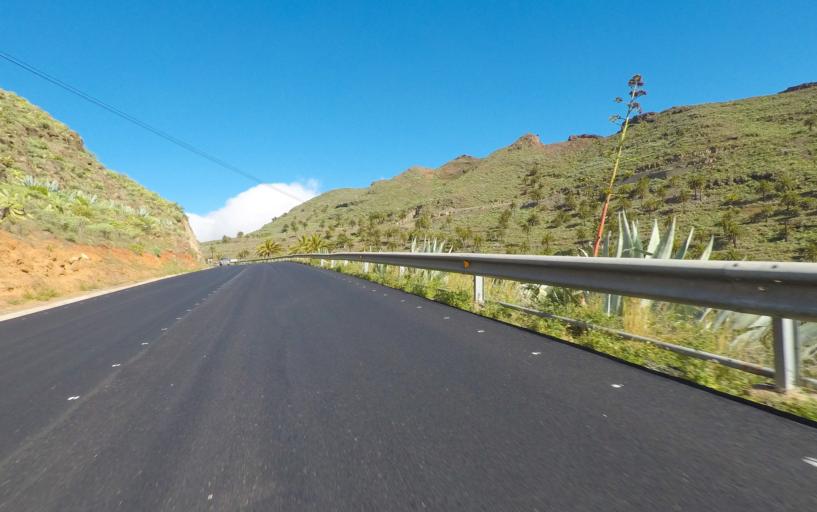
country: ES
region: Canary Islands
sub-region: Provincia de Santa Cruz de Tenerife
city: Alajero
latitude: 28.0734
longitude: -17.2073
